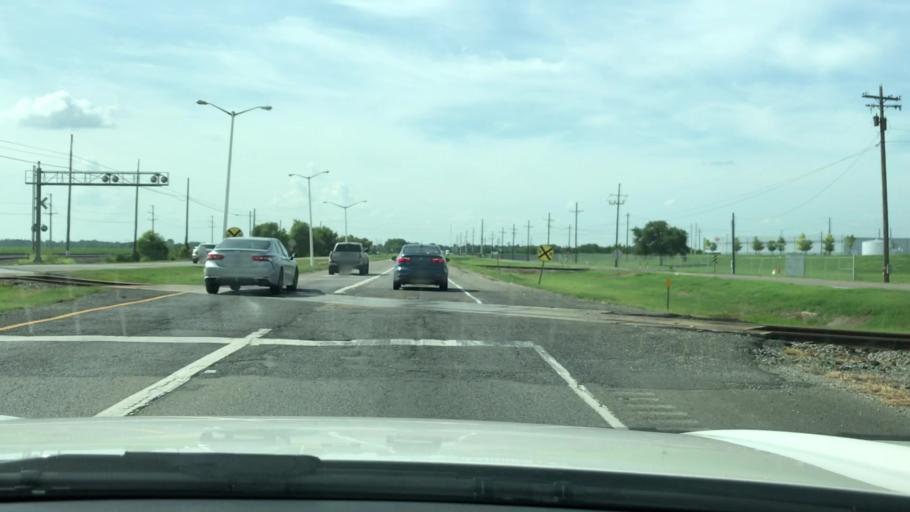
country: US
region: Louisiana
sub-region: West Baton Rouge Parish
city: Addis
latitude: 30.3327
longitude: -91.2570
